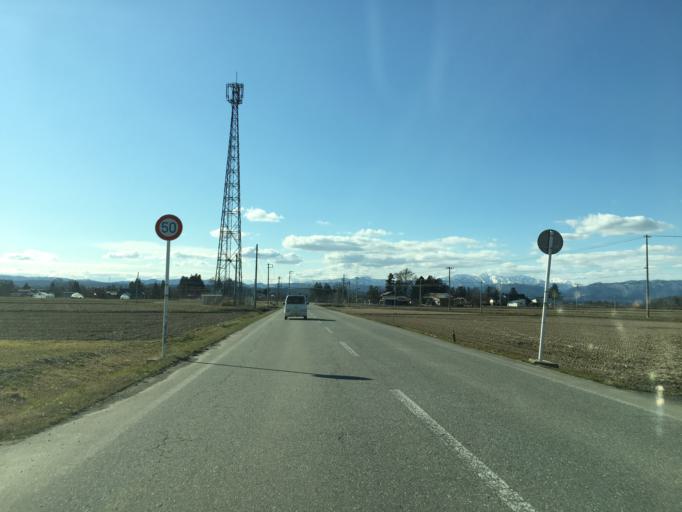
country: JP
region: Yamagata
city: Yonezawa
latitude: 38.0098
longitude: 140.0871
